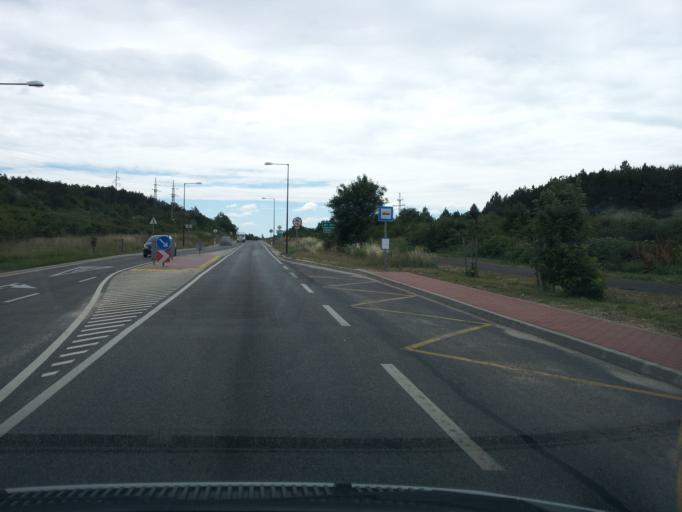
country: HU
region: Veszprem
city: Liter
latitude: 47.0968
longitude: 18.0188
